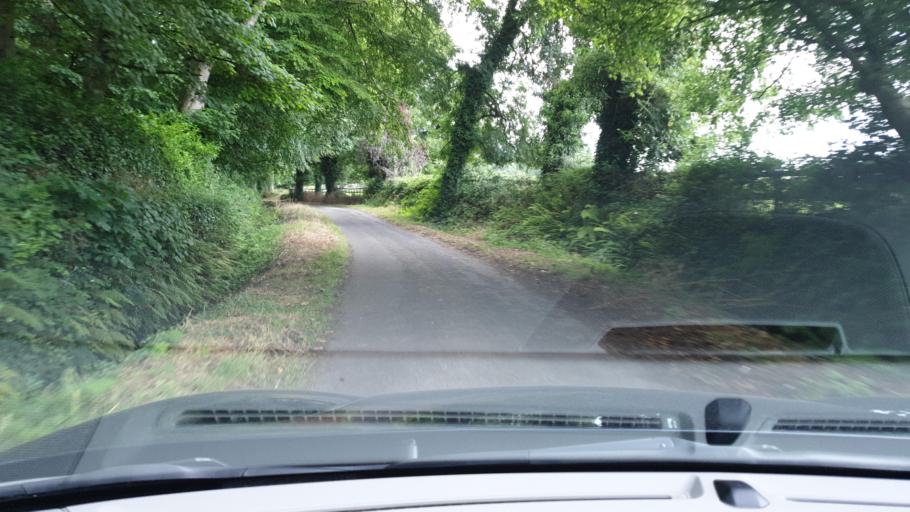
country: IE
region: Leinster
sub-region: An Mhi
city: Ashbourne
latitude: 53.5513
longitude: -6.3865
